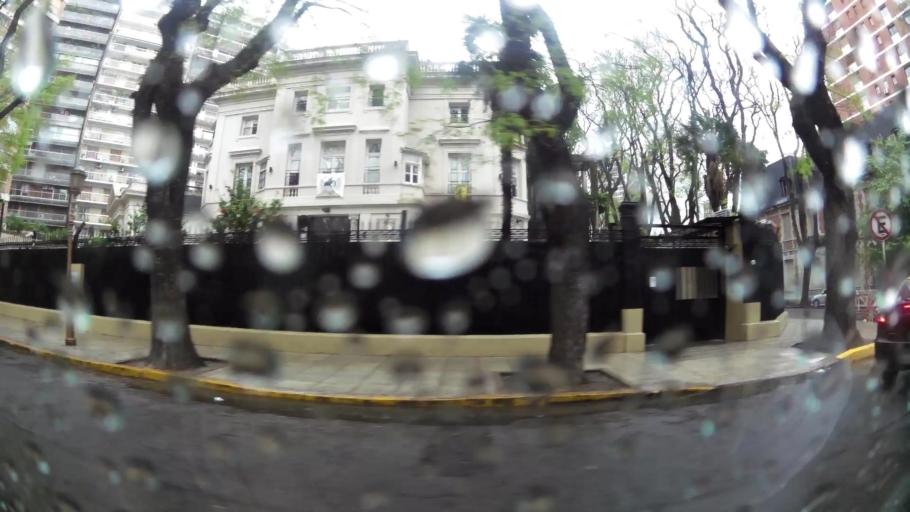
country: AR
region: Buenos Aires F.D.
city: Retiro
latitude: -34.5801
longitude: -58.4031
